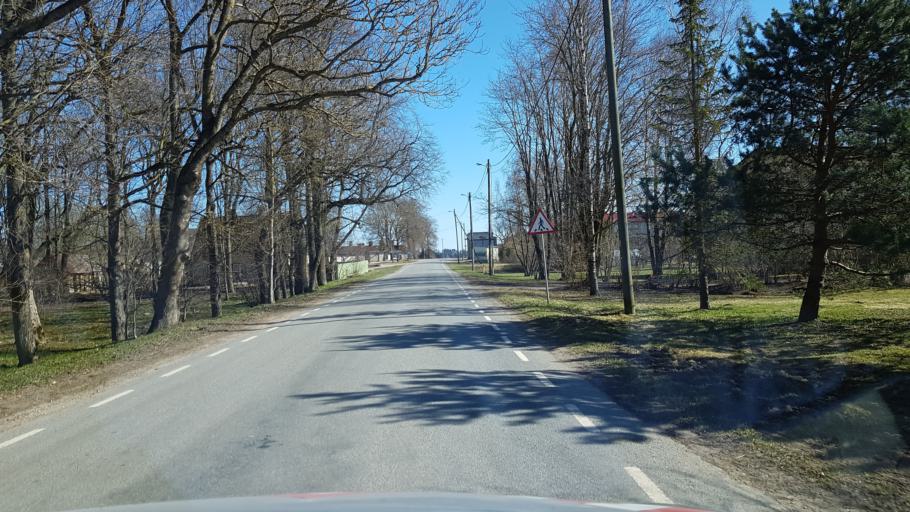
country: EE
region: Laeaene-Virumaa
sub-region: Someru vald
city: Someru
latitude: 59.3420
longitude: 26.5097
